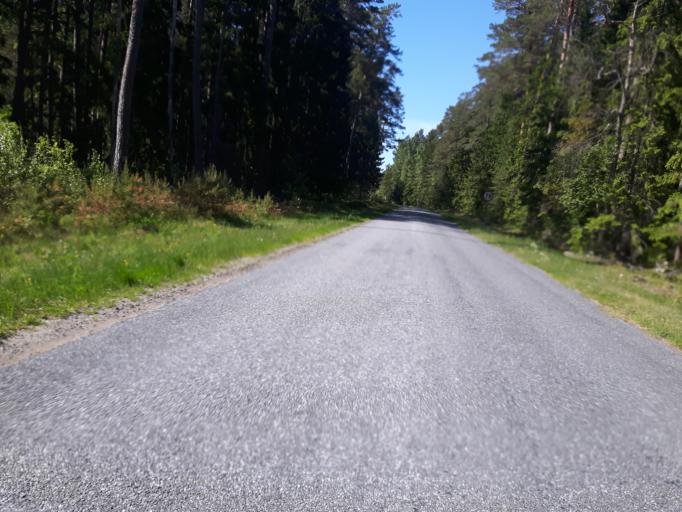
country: EE
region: Laeaene-Virumaa
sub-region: Haljala vald
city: Haljala
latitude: 59.5744
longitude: 26.2793
